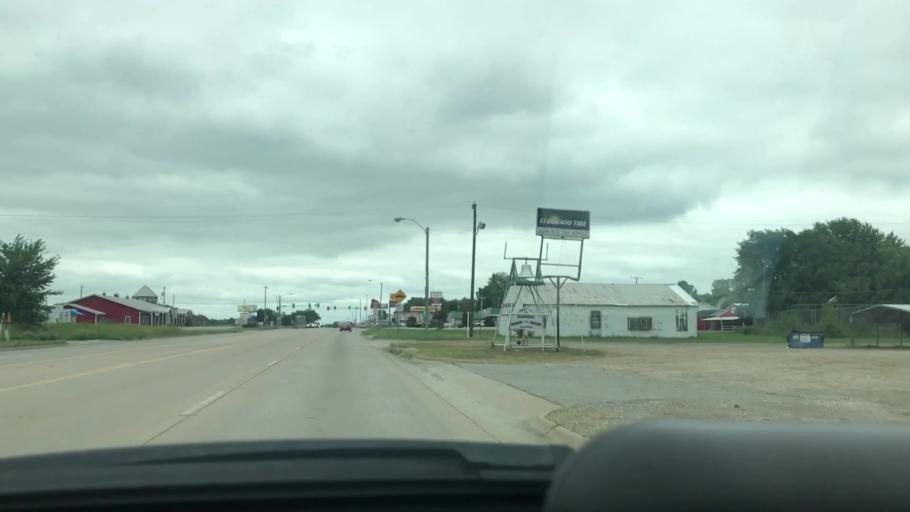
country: US
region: Oklahoma
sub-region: Mayes County
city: Chouteau
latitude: 36.1840
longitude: -95.3429
